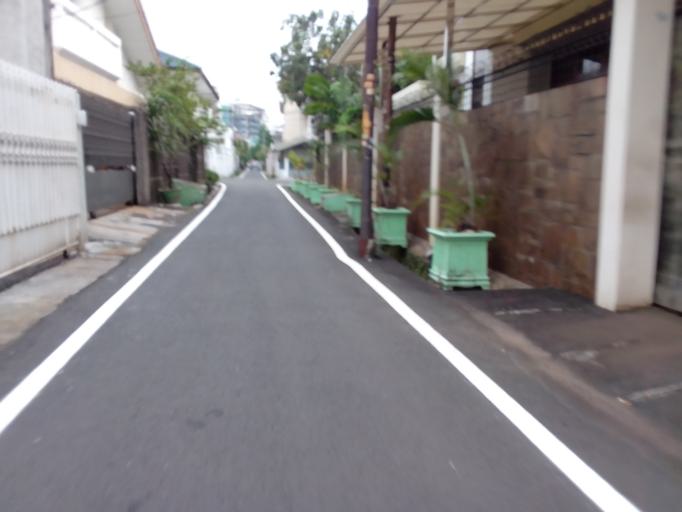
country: ID
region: Jakarta Raya
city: Jakarta
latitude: -6.1719
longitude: 106.8135
